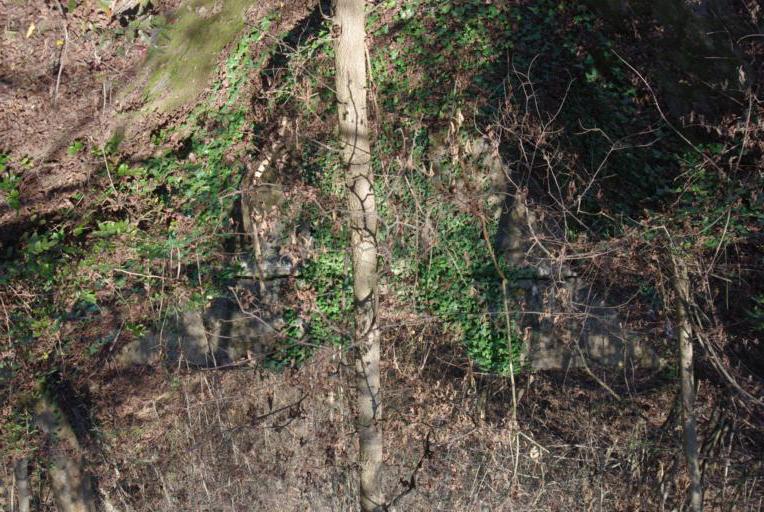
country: HU
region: Pest
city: Urom
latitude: 47.5827
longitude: 19.0348
